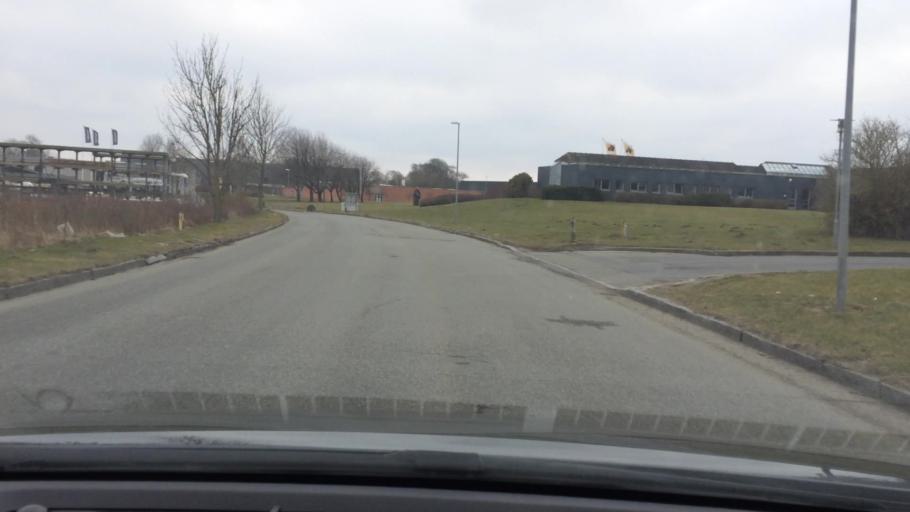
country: DK
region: South Denmark
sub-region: Vejle Kommune
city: Vejle
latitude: 55.7327
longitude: 9.5676
